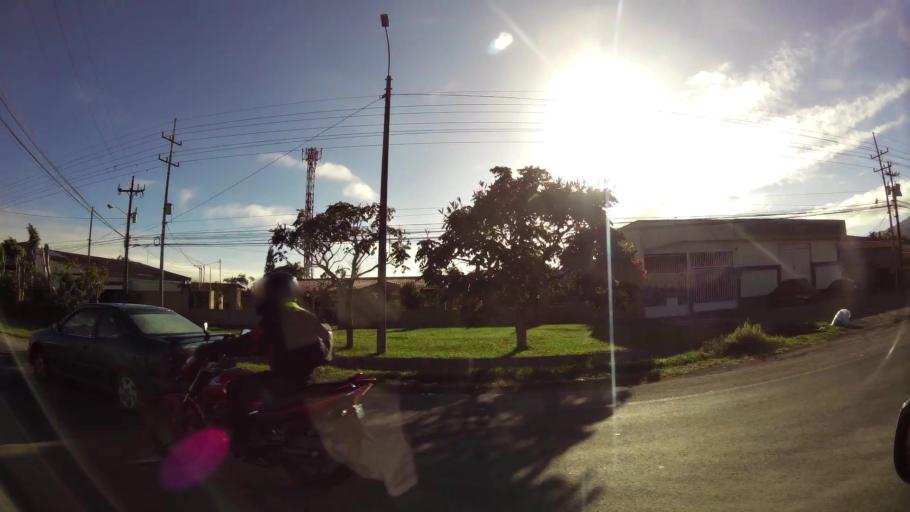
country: CR
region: Cartago
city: Tobosi
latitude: 9.8417
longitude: -83.9507
